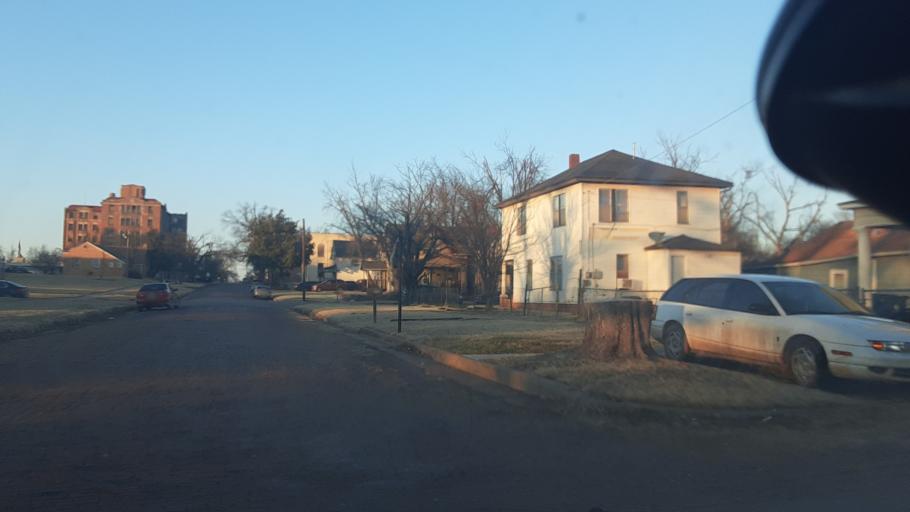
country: US
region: Oklahoma
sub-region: Logan County
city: Guthrie
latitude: 35.8754
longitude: -97.4215
